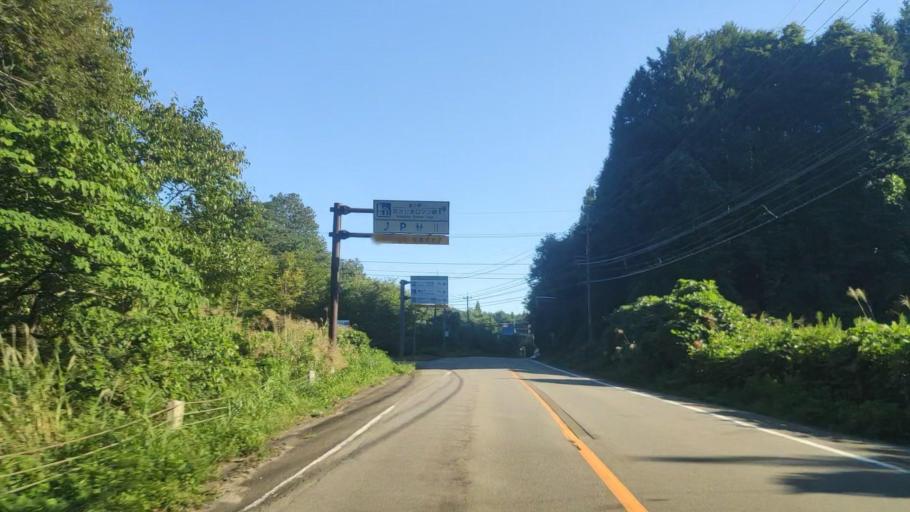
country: JP
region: Ishikawa
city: Nanao
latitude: 37.1335
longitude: 136.8631
